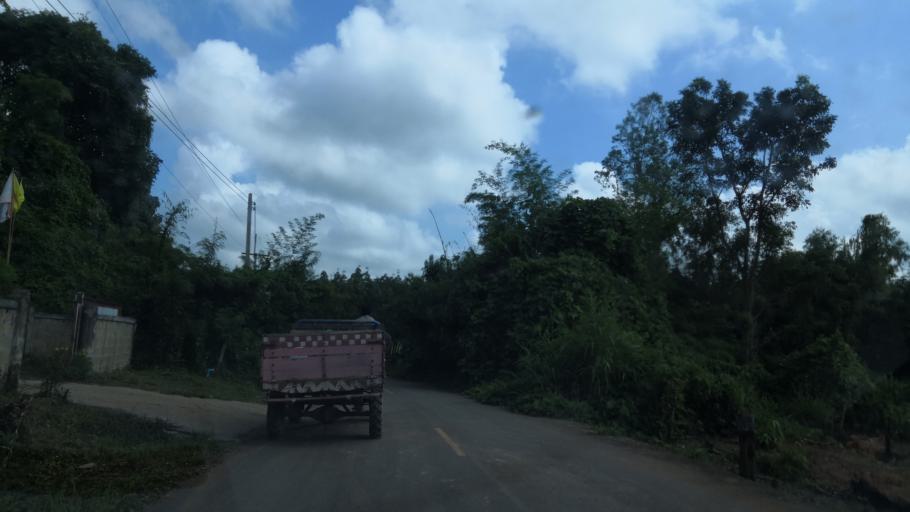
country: TH
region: Chiang Rai
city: Wiang Chiang Rung
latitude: 20.0206
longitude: 100.0433
